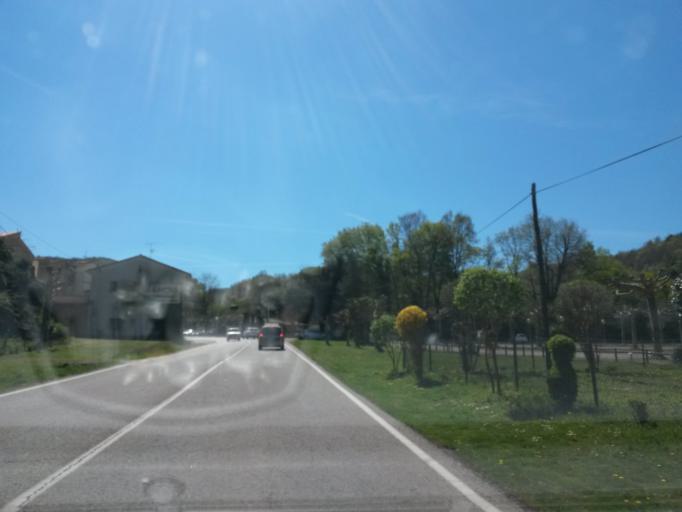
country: ES
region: Catalonia
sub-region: Provincia de Girona
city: Sant Cristofol de les Fonts
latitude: 42.1490
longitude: 2.5300
